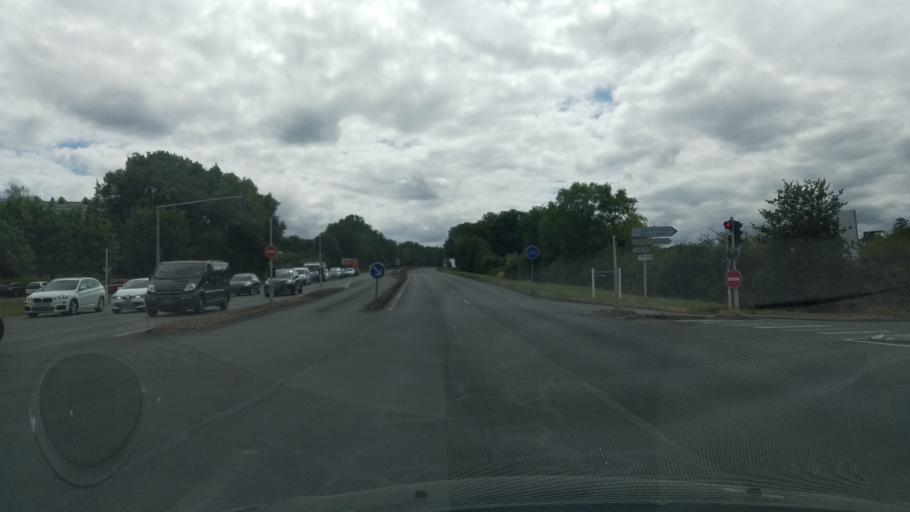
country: FR
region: Poitou-Charentes
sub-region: Departement de la Vienne
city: Saint-Benoit
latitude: 46.5546
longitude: 0.3339
